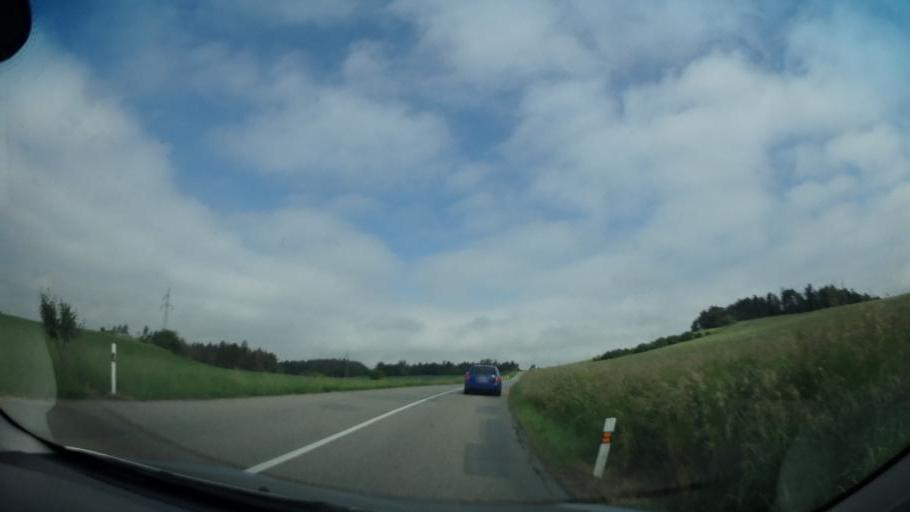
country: CZ
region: South Moravian
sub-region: Okres Brno-Venkov
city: Dolni Loucky
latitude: 49.3808
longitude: 16.3435
